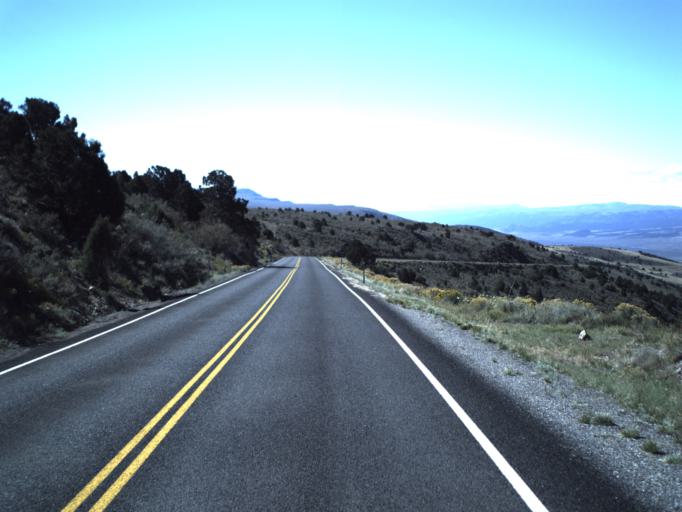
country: US
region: Utah
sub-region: Wayne County
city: Loa
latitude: 38.4826
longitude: -111.8242
